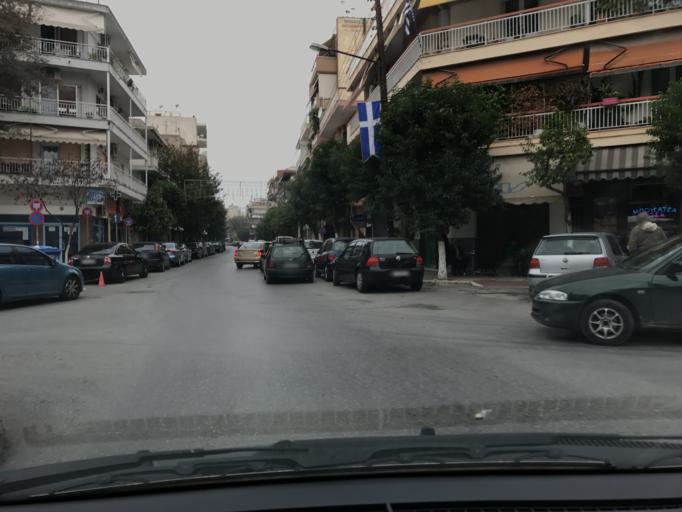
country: GR
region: Central Macedonia
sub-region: Nomos Thessalonikis
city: Ampelokipoi
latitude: 40.6516
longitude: 22.9277
